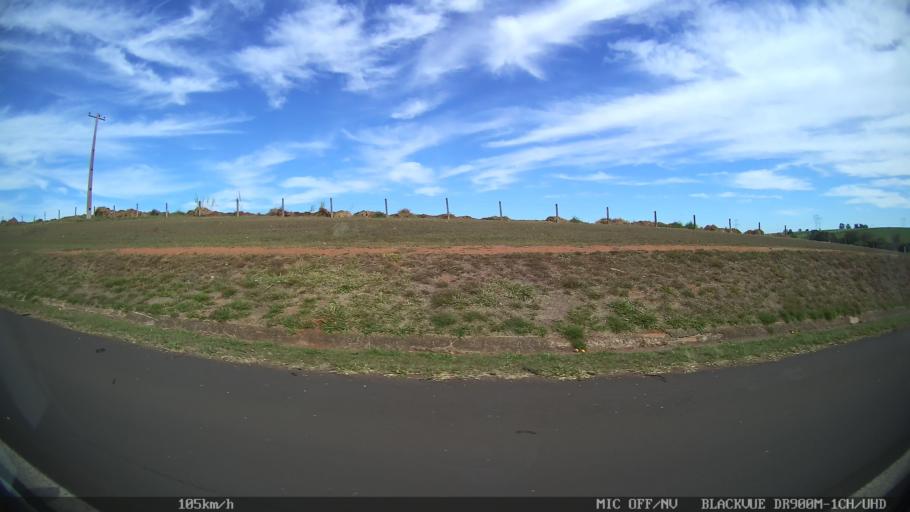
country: BR
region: Sao Paulo
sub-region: Matao
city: Matao
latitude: -21.5649
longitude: -48.4695
